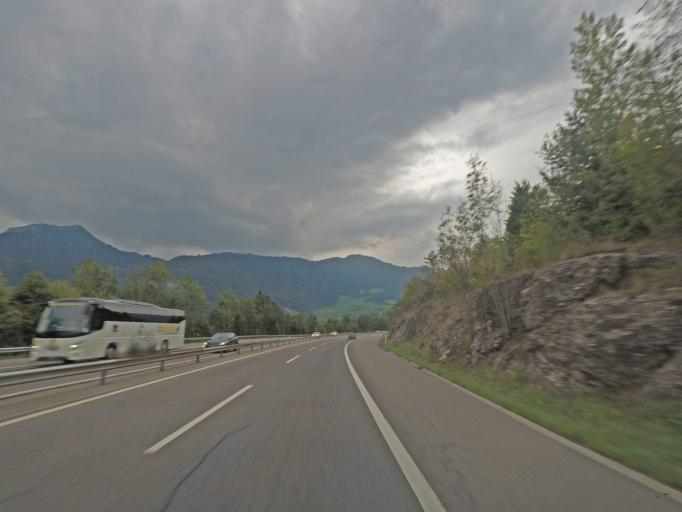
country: CH
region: Schwyz
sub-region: Bezirk Schwyz
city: Steinen
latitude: 47.0464
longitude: 8.5835
